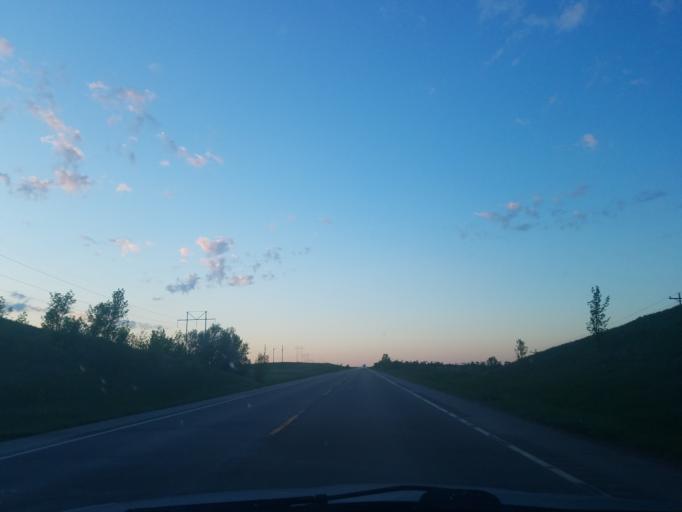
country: US
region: North Dakota
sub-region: McKenzie County
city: Watford City
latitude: 47.6816
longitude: -103.2838
